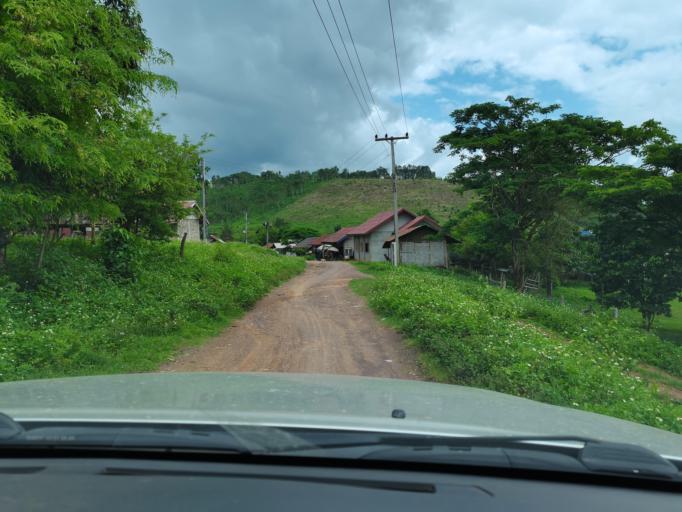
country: LA
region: Loungnamtha
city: Muang Long
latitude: 20.7062
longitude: 101.0098
